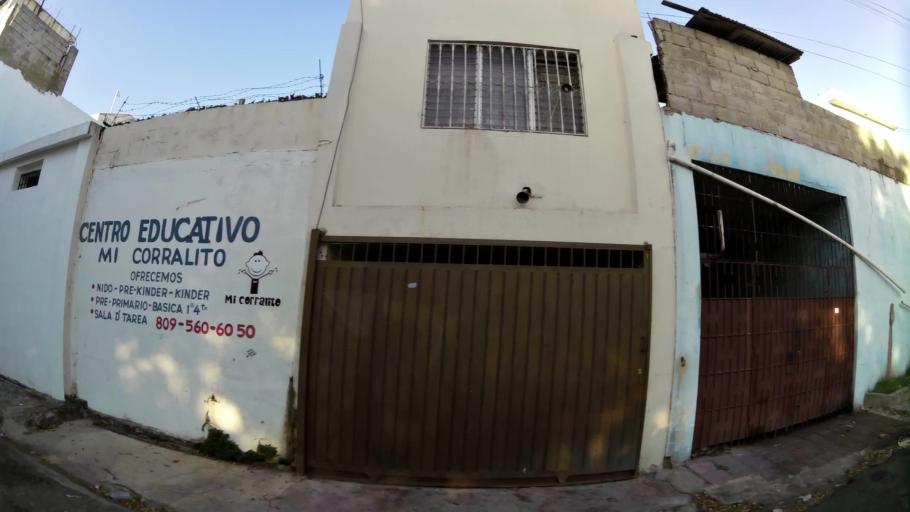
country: DO
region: Nacional
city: Santo Domingo
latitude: 18.4849
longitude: -69.9688
